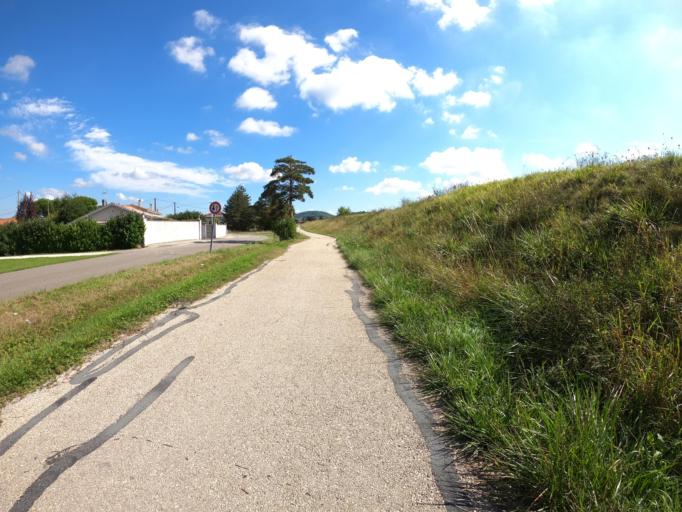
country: FR
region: Aquitaine
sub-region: Departement du Lot-et-Garonne
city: Pujols
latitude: 44.3952
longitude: 0.6895
